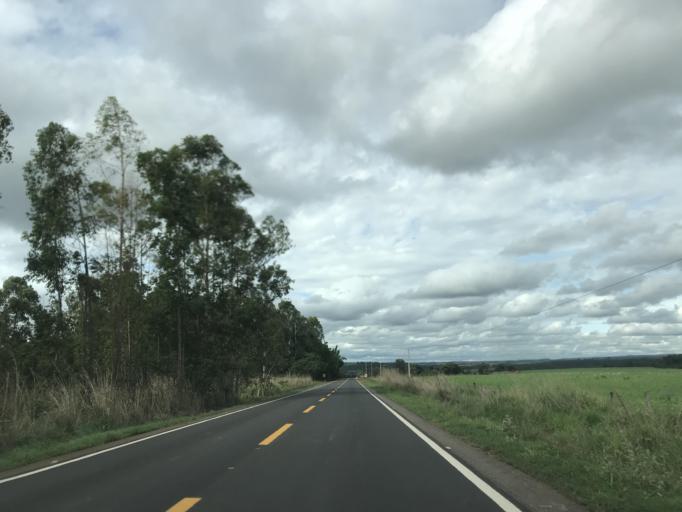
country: BR
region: Goias
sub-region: Bela Vista De Goias
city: Bela Vista de Goias
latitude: -17.1832
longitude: -48.6896
